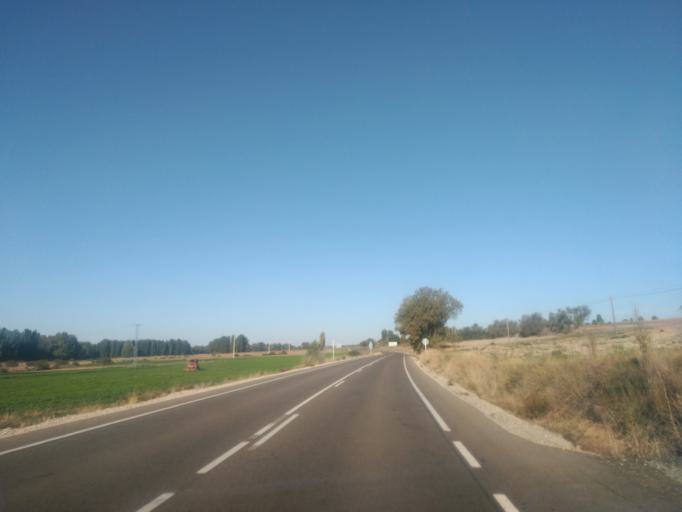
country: ES
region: Castille and Leon
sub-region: Provincia de Burgos
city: Penaranda de Duero
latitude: 41.6855
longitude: -3.4945
